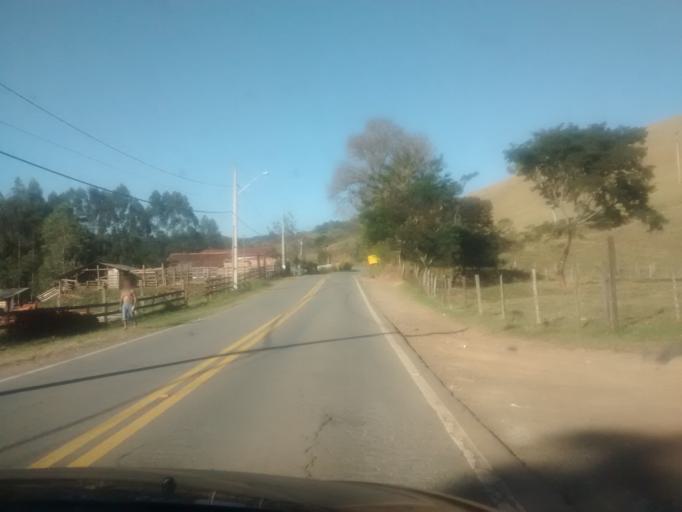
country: BR
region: Sao Paulo
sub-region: Campos Do Jordao
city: Campos do Jordao
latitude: -22.8264
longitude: -45.7194
